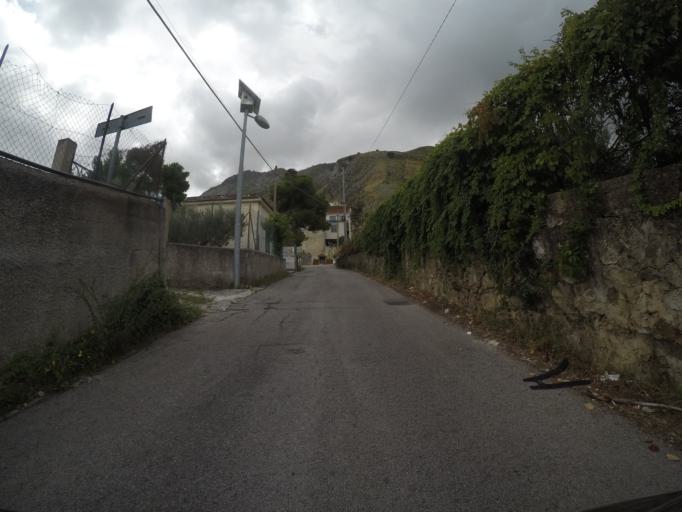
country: IT
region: Sicily
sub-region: Palermo
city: Montelepre
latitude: 38.1219
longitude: 13.1846
